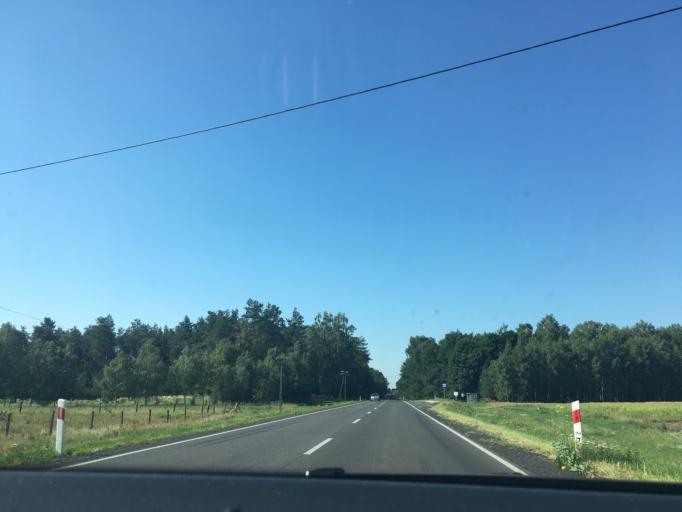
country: PL
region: Lublin Voivodeship
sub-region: Powiat lubartowski
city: Kock
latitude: 51.6713
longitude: 22.4782
